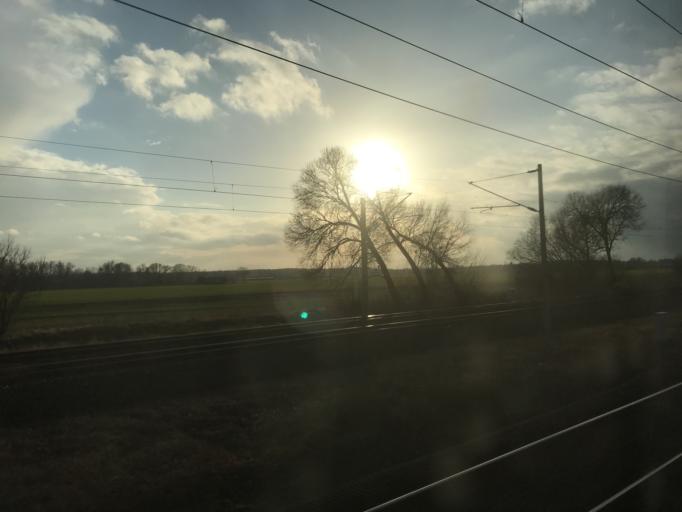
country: DE
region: Brandenburg
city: Falkensee
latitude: 52.5405
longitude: 13.1034
